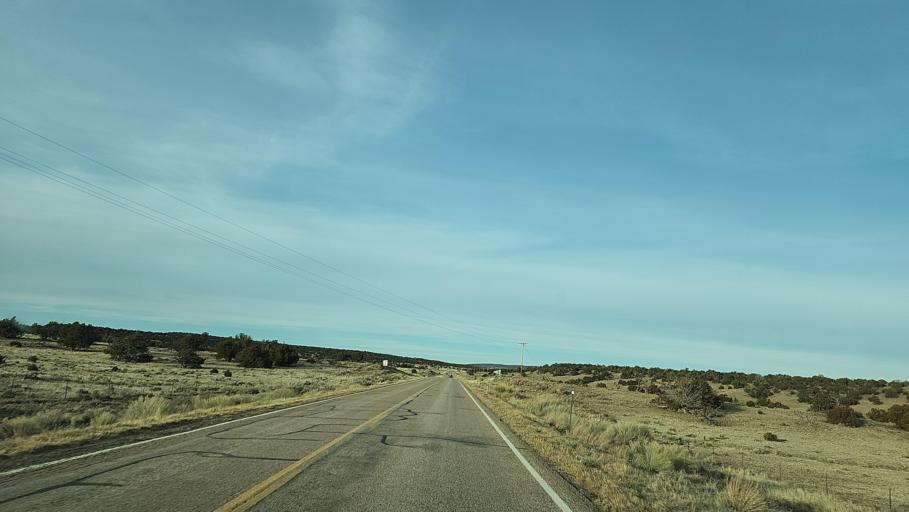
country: US
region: New Mexico
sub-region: Catron County
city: Reserve
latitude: 34.3904
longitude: -108.4484
